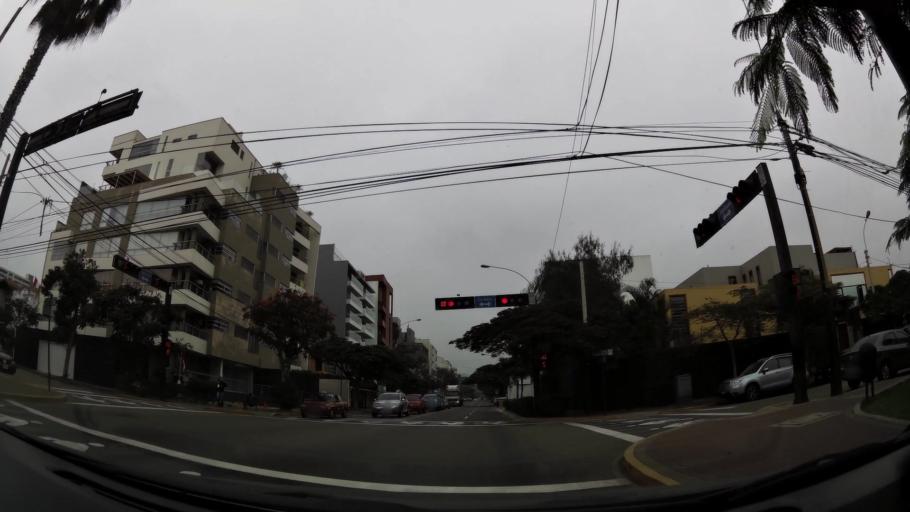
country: PE
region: Lima
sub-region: Lima
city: San Isidro
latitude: -12.0956
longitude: -77.0426
